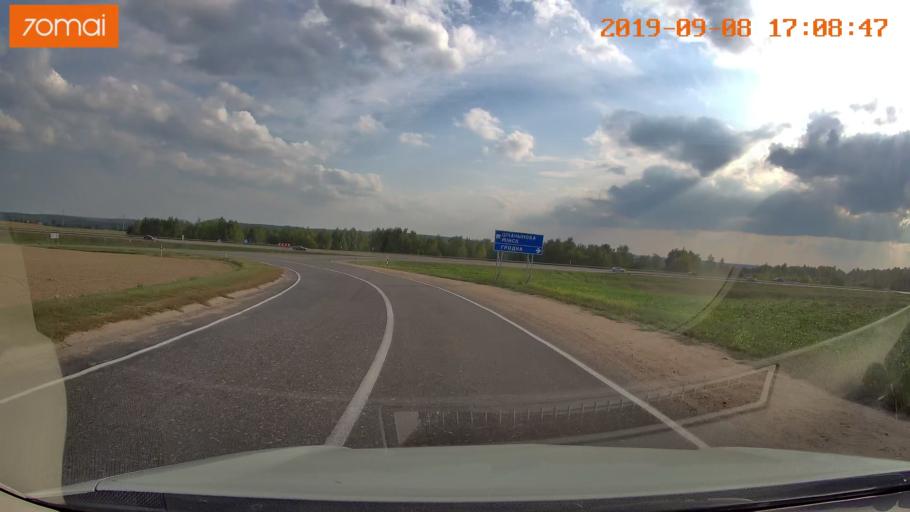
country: BY
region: Grodnenskaya
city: Hrodna
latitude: 53.6554
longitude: 23.9628
